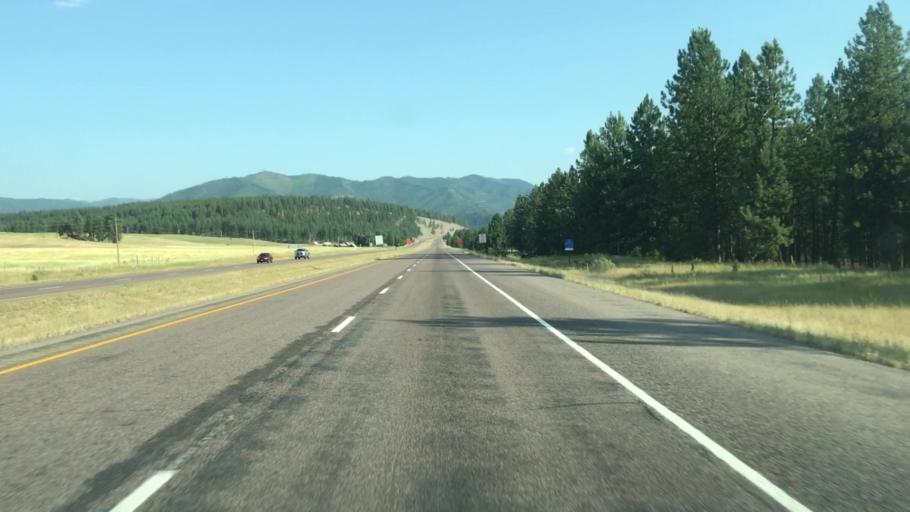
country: US
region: Montana
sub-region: Mineral County
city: Superior
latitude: 47.0367
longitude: -114.7468
